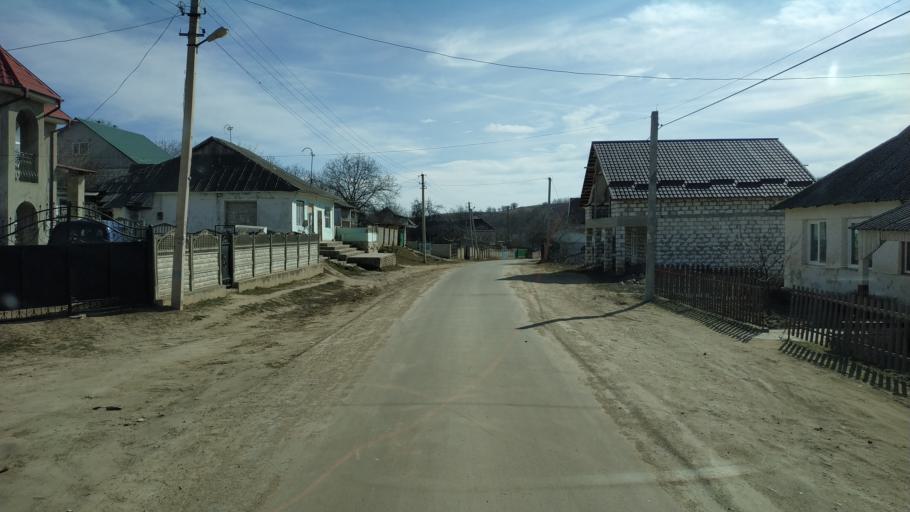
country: MD
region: Nisporeni
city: Nisporeni
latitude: 47.0961
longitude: 28.2975
